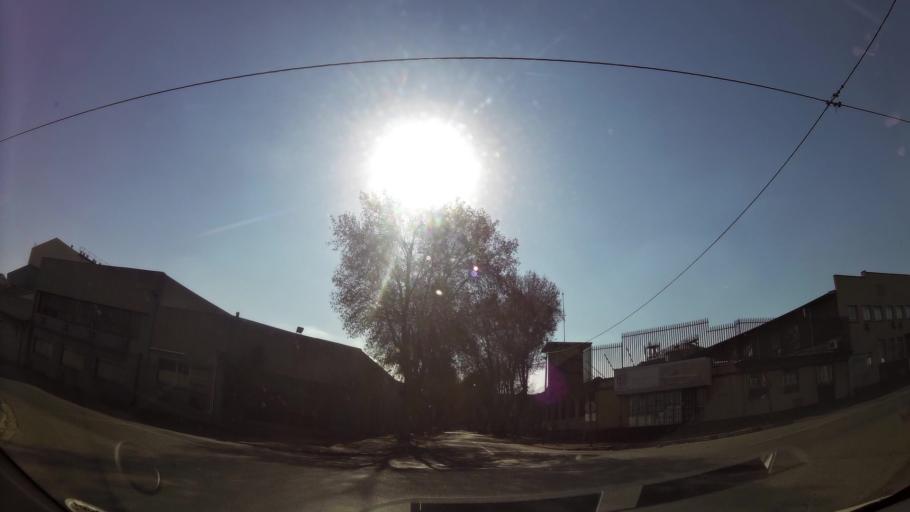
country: ZA
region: Gauteng
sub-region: City of Johannesburg Metropolitan Municipality
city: Johannesburg
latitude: -26.1993
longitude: 27.9765
